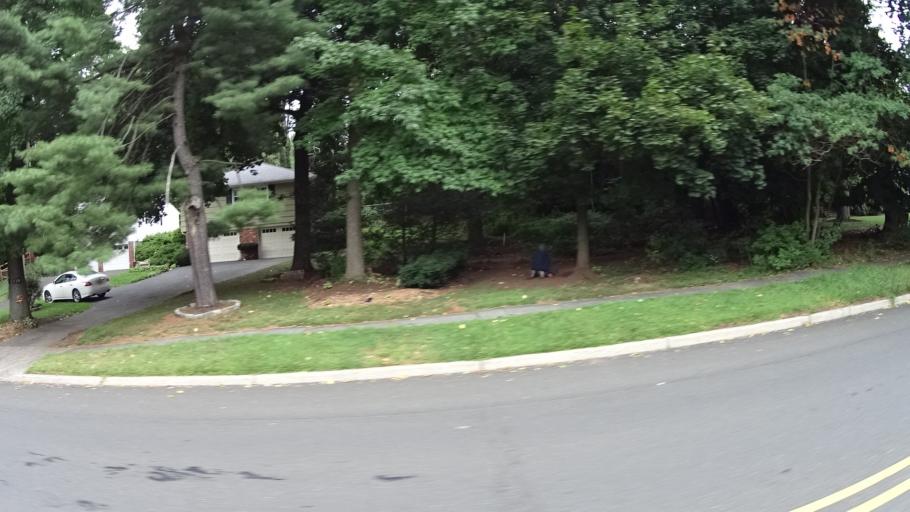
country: US
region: New Jersey
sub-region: Union County
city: New Providence
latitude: 40.7119
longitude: -74.3801
